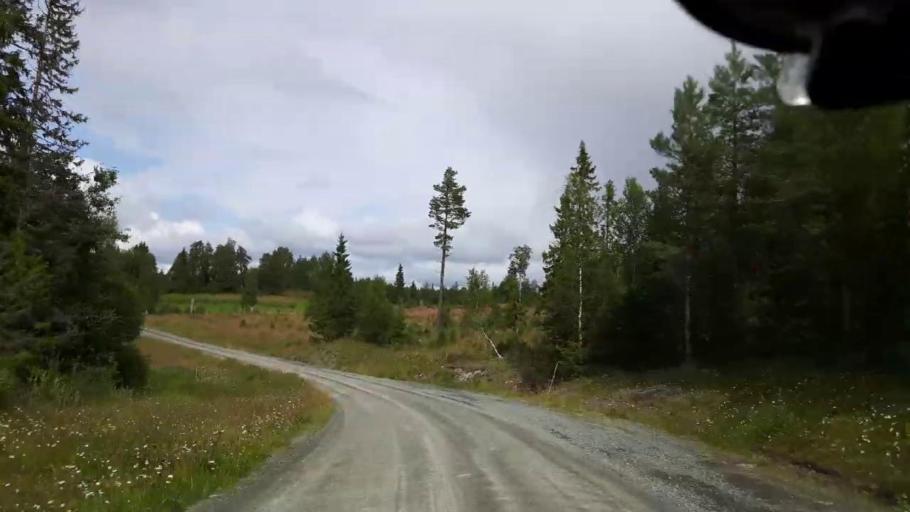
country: SE
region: Jaemtland
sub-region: Krokoms Kommun
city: Valla
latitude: 63.5632
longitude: 13.9165
